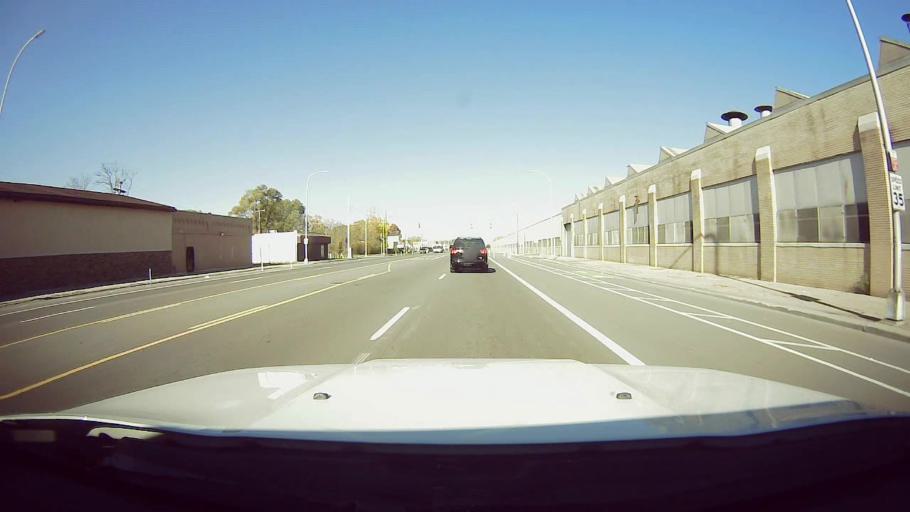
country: US
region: Michigan
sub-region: Wayne County
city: Dearborn
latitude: 42.3485
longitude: -83.1331
